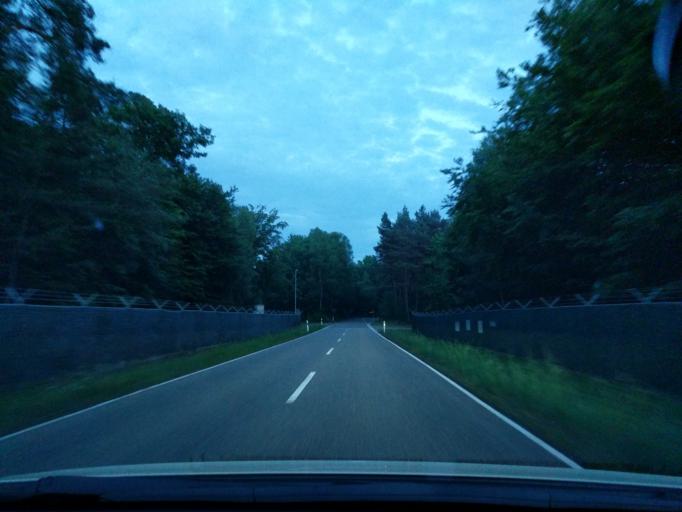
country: DE
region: Rheinland-Pfalz
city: Rodenbach
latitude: 49.4451
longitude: 7.6479
